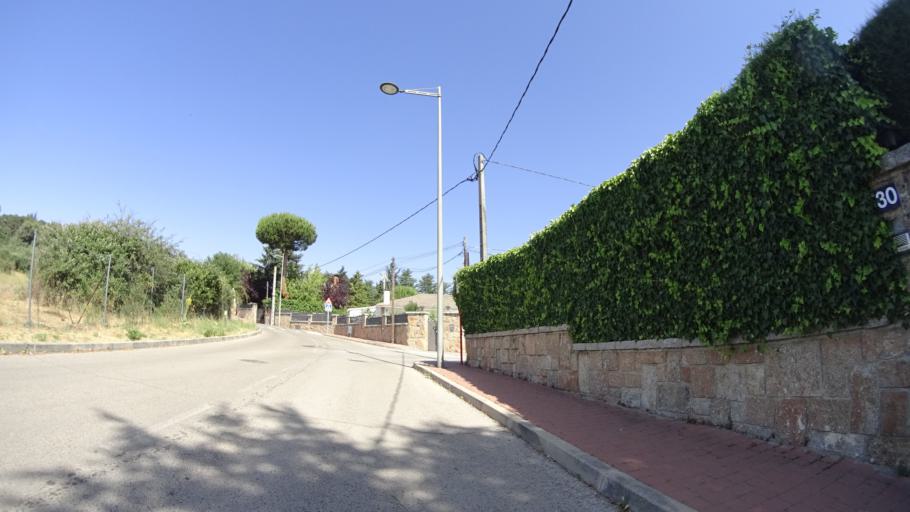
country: ES
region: Madrid
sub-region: Provincia de Madrid
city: Guadarrama
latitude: 40.6800
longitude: -4.1010
